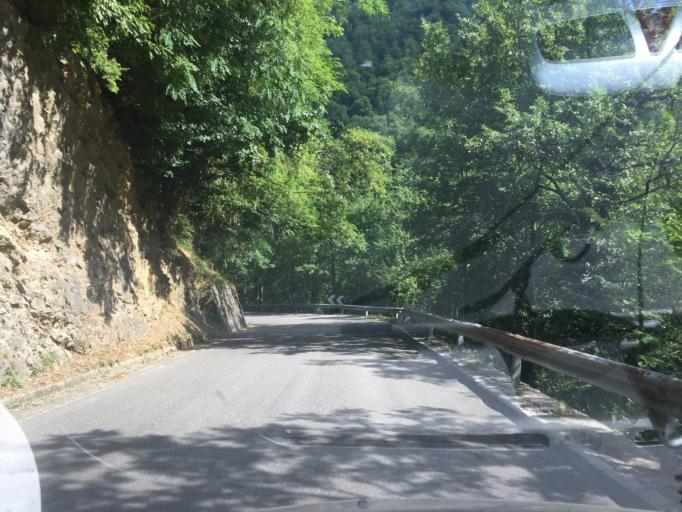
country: IT
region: Tuscany
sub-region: Provincia di Lucca
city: Careggine
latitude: 44.1316
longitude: 10.3090
